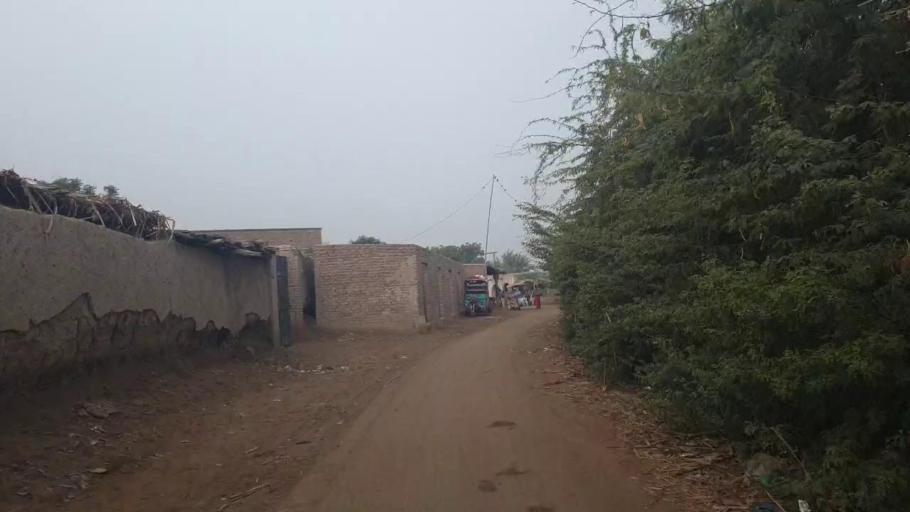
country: PK
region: Sindh
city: Tando Adam
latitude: 25.7108
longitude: 68.6471
